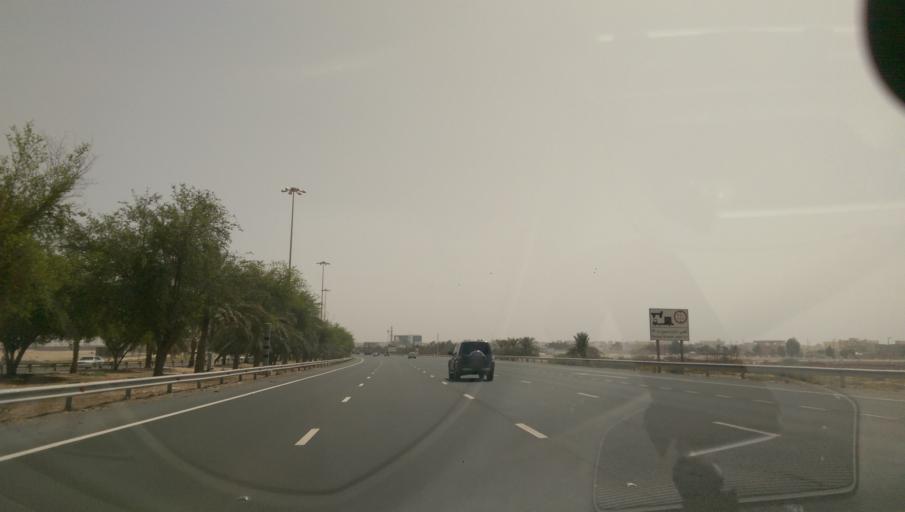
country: AE
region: Abu Dhabi
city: Abu Dhabi
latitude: 24.3305
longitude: 54.6284
